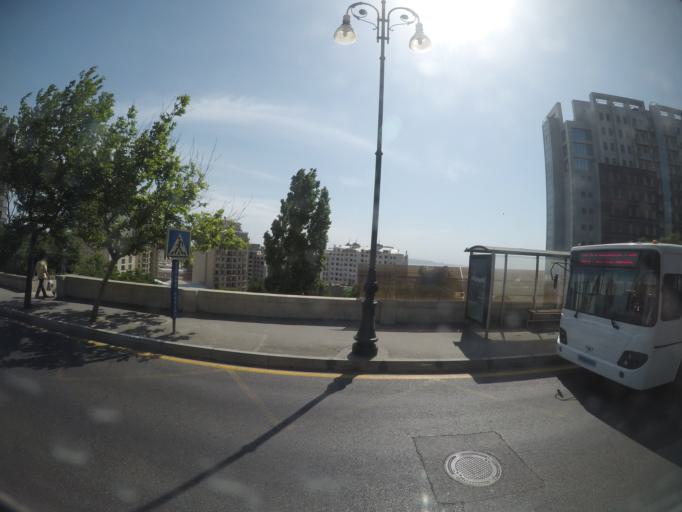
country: AZ
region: Baki
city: Badamdar
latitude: 40.3675
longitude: 49.8249
